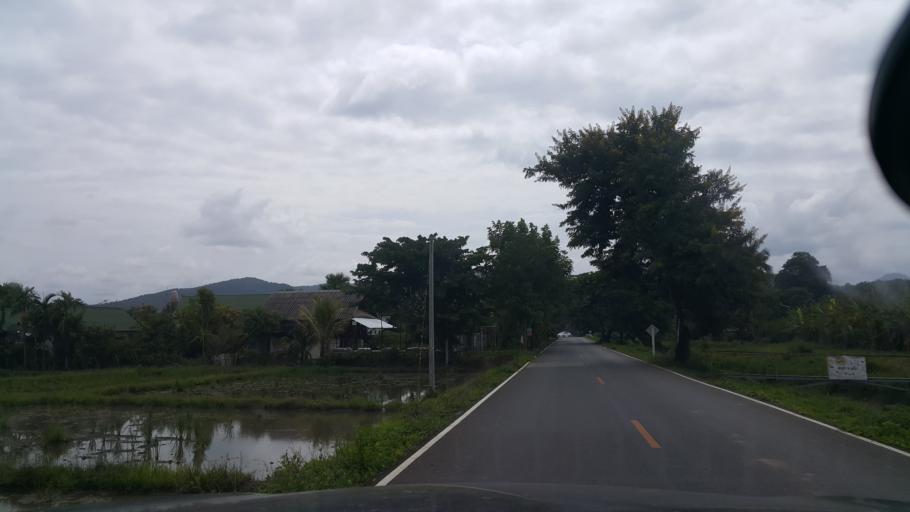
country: TH
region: Chiang Mai
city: San Kamphaeng
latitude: 18.7531
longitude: 99.1684
